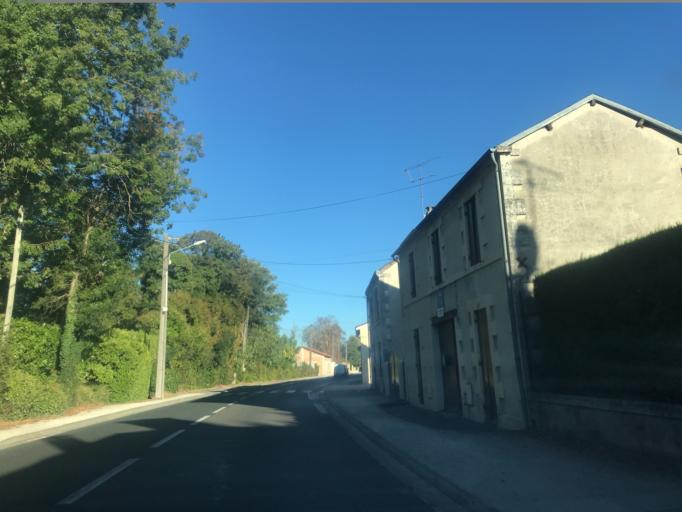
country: FR
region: Poitou-Charentes
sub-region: Departement de la Charente-Maritime
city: Saint-Aigulin
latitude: 45.1574
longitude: -0.0060
